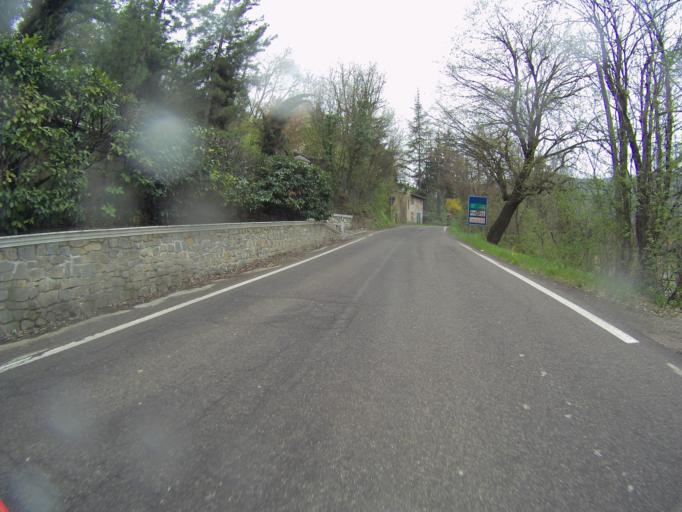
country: IT
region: Emilia-Romagna
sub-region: Provincia di Reggio Emilia
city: Ciano d'Enza
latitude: 44.5718
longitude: 10.4060
